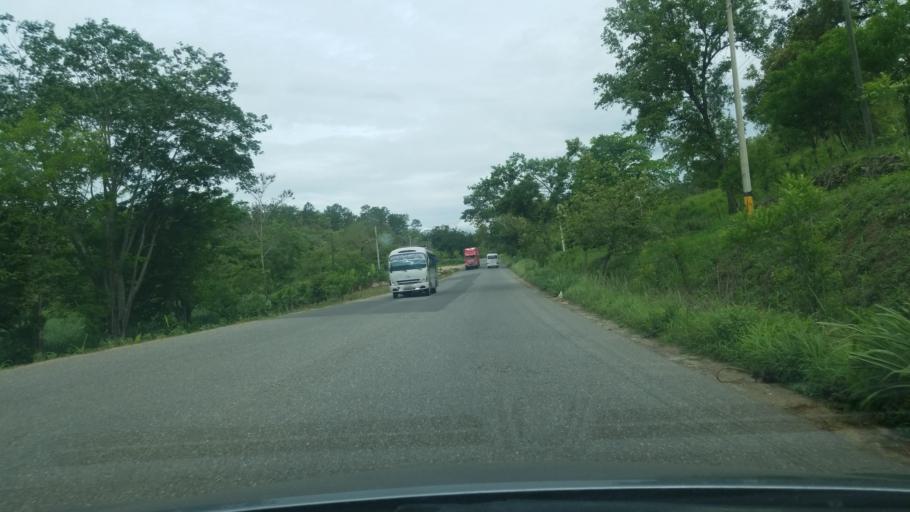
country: HN
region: Santa Barbara
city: San Marcos
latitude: 15.3036
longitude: -88.4462
